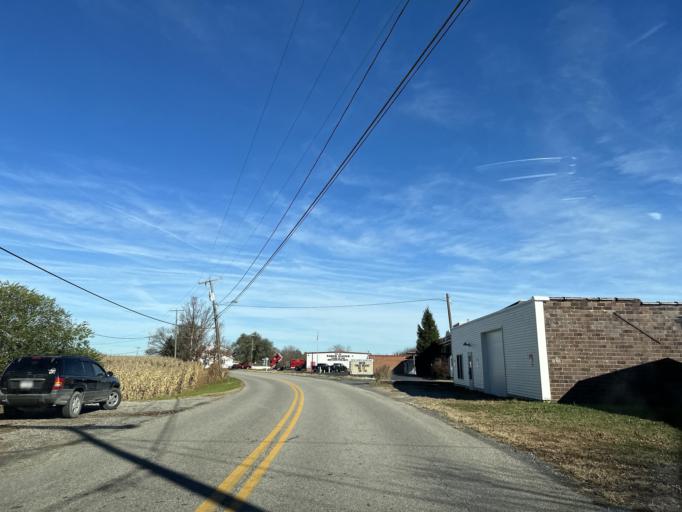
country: US
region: Virginia
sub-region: Augusta County
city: Crimora
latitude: 38.2003
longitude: -78.9044
